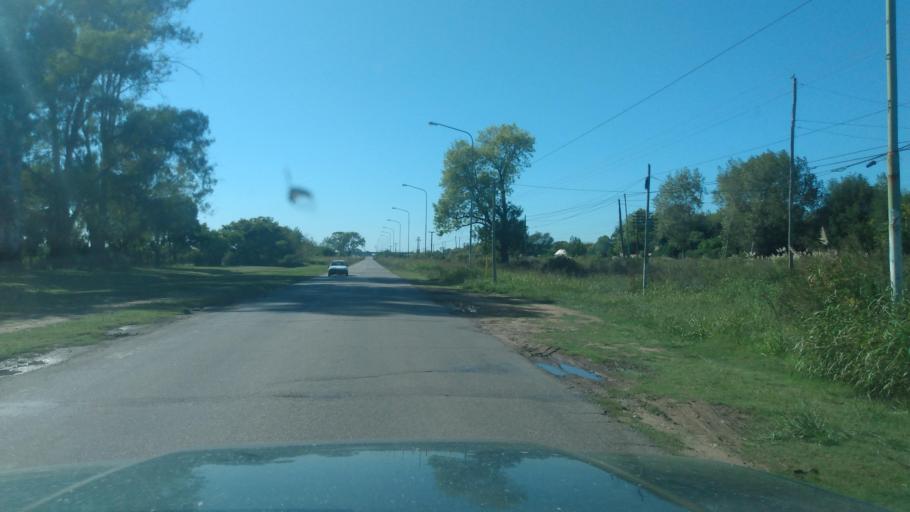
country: AR
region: Buenos Aires
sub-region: Partido de Lujan
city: Lujan
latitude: -34.5856
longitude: -59.0514
